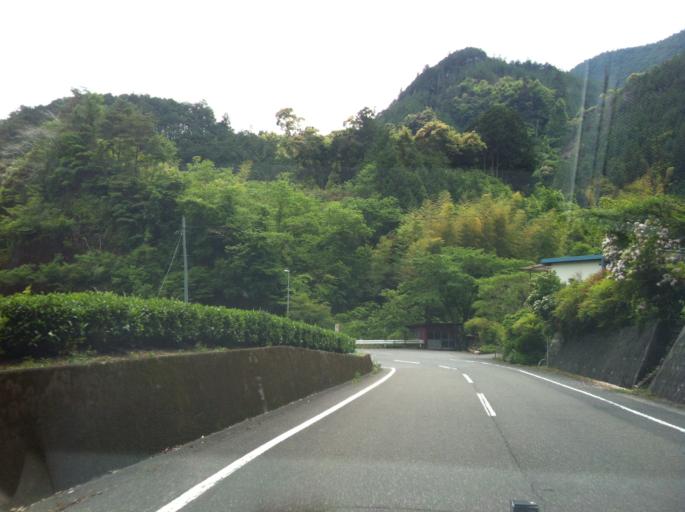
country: JP
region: Shizuoka
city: Shizuoka-shi
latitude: 35.1250
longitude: 138.3235
